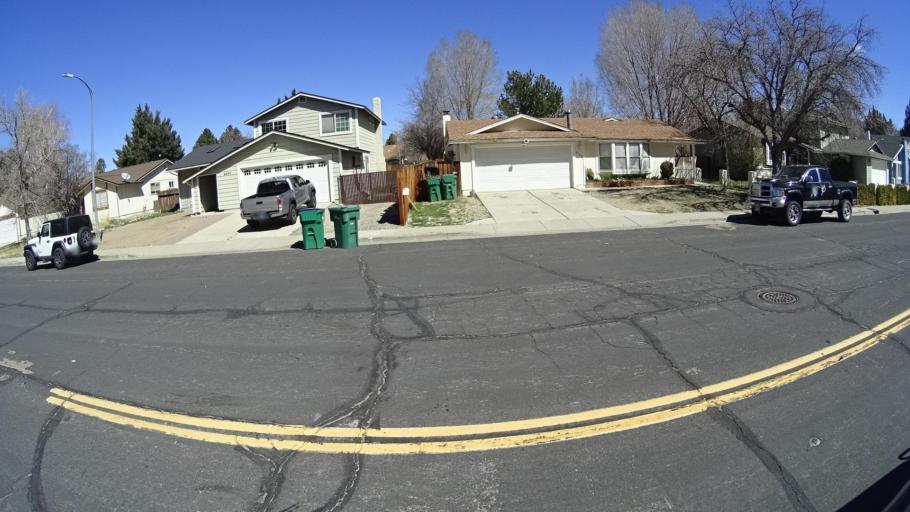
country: US
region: Nevada
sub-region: Washoe County
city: Sparks
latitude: 39.4743
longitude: -119.7522
